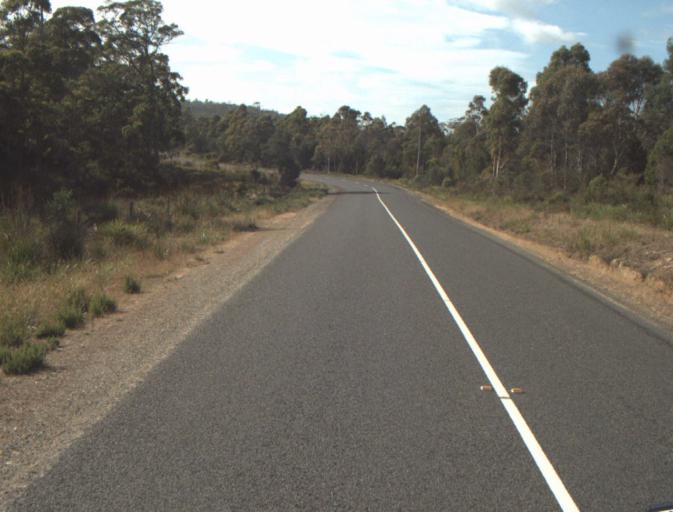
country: AU
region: Tasmania
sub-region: Dorset
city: Bridport
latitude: -41.1354
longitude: 147.2230
